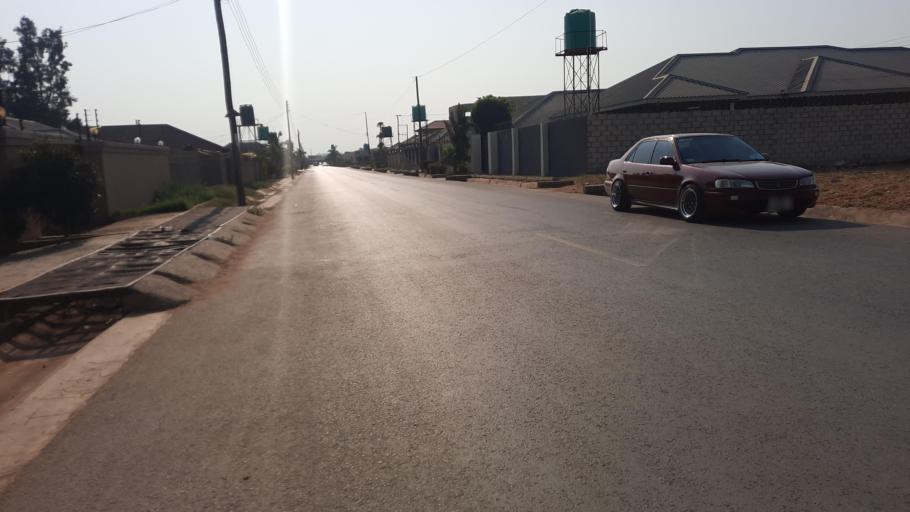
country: ZM
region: Lusaka
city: Lusaka
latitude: -15.3901
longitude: 28.3859
